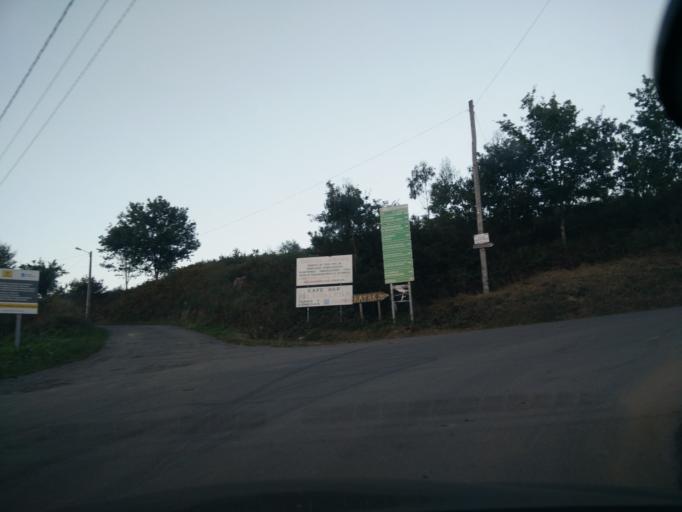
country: ES
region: Galicia
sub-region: Provincia da Coruna
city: Monfero
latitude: 43.3422
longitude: -8.0375
